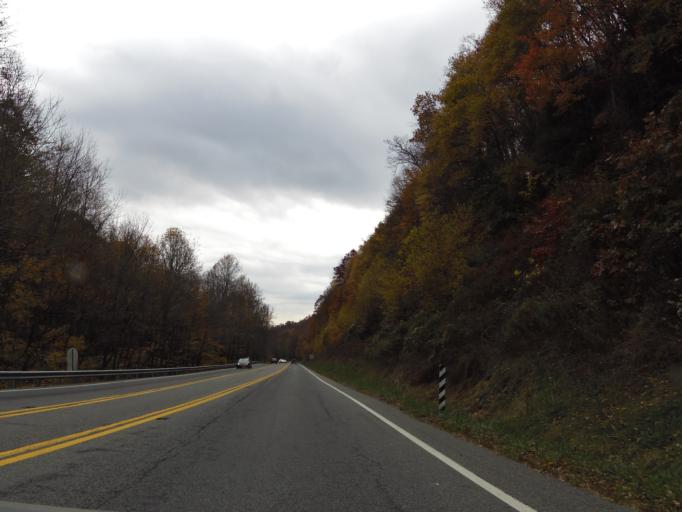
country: US
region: Virginia
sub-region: Carroll County
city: Cana
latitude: 36.6633
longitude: -80.6927
